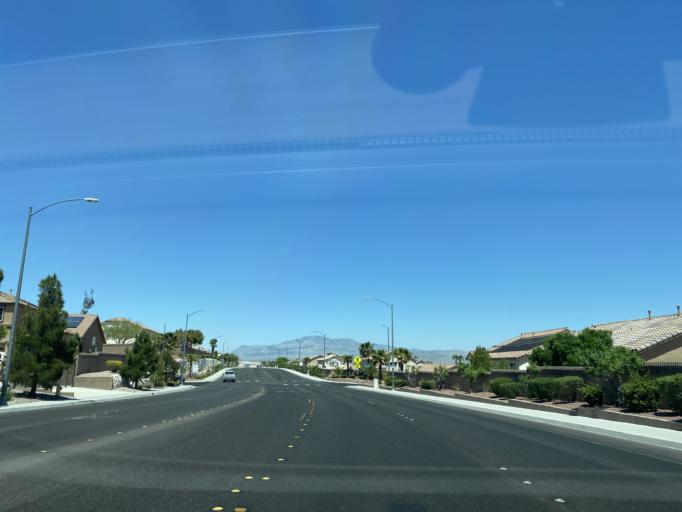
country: US
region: Nevada
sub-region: Clark County
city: Summerlin South
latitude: 36.2412
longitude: -115.3280
